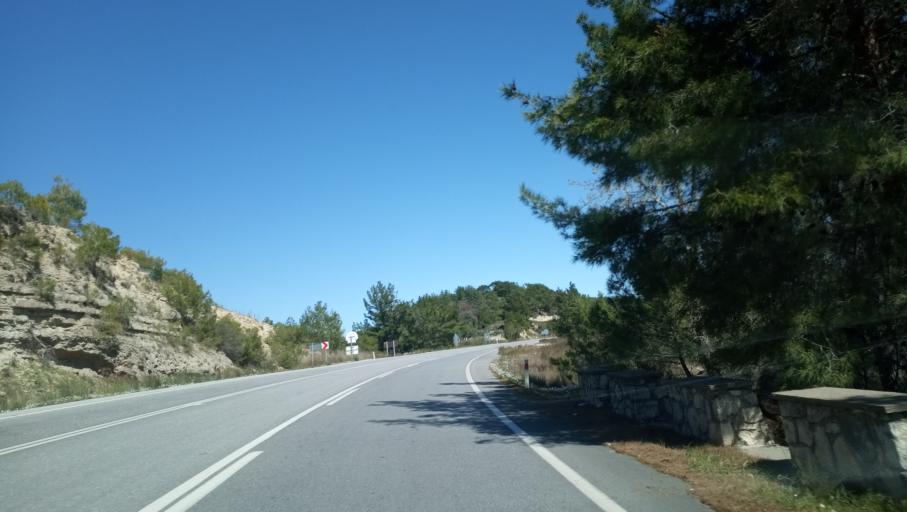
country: TR
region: Antalya
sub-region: Manavgat
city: Kizilagac
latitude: 36.7522
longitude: 31.6233
